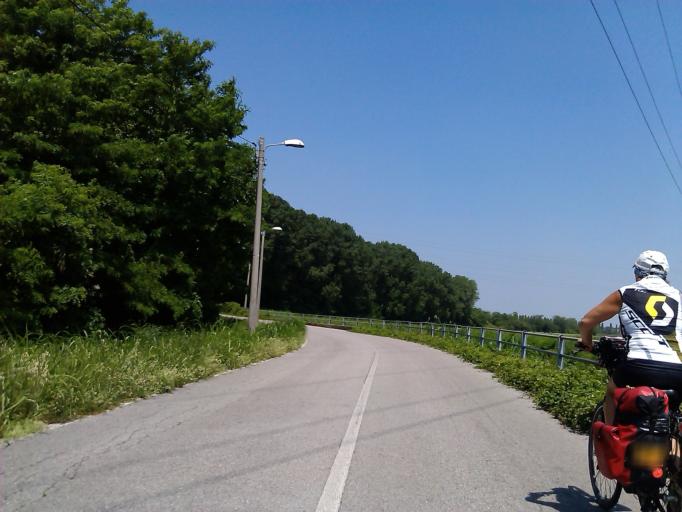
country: IT
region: Veneto
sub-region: Provincia di Venezia
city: Fornase
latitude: 45.4574
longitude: 12.1944
